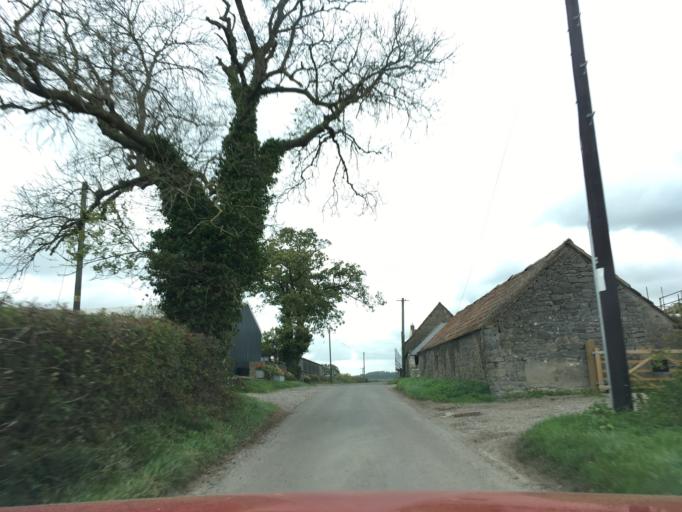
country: GB
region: England
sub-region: South Gloucestershire
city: Wickwar
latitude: 51.5989
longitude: -2.3822
